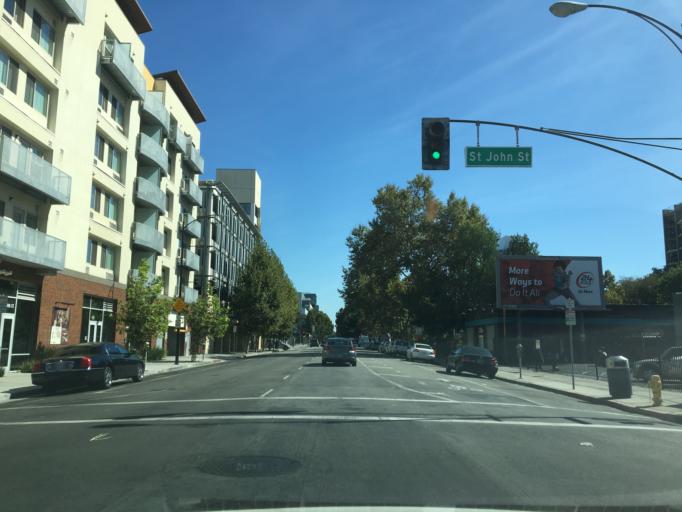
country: US
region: California
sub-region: Santa Clara County
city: San Jose
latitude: 37.3392
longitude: -121.8886
